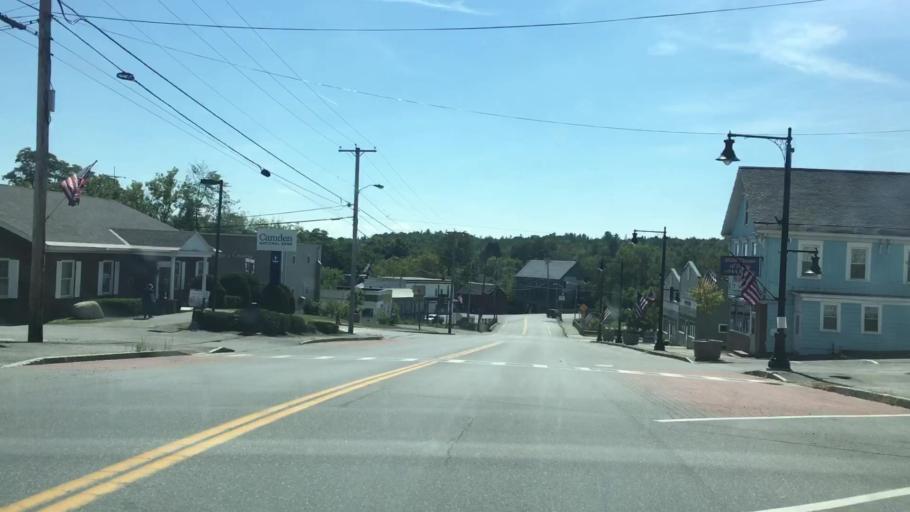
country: US
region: Maine
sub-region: Piscataquis County
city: Milo
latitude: 45.2528
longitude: -68.9864
